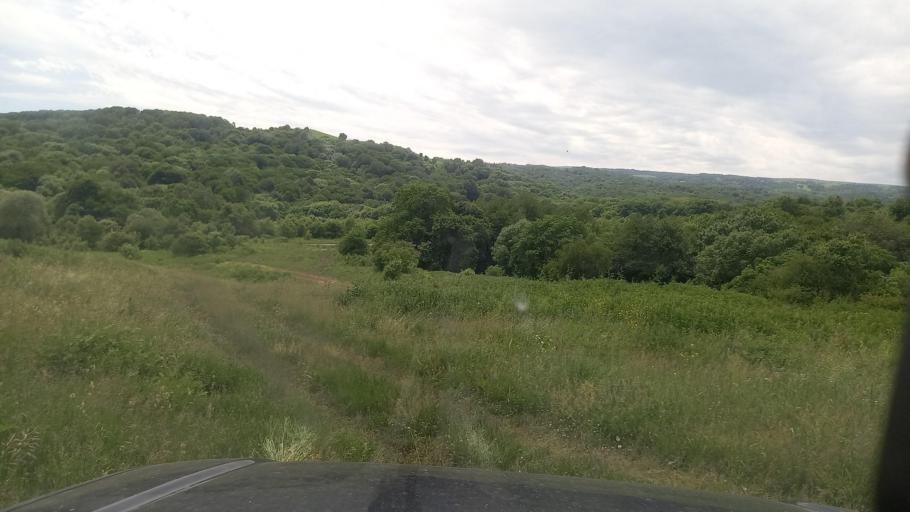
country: RU
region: Karachayevo-Cherkesiya
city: Pregradnaya
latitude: 44.0957
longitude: 41.1663
